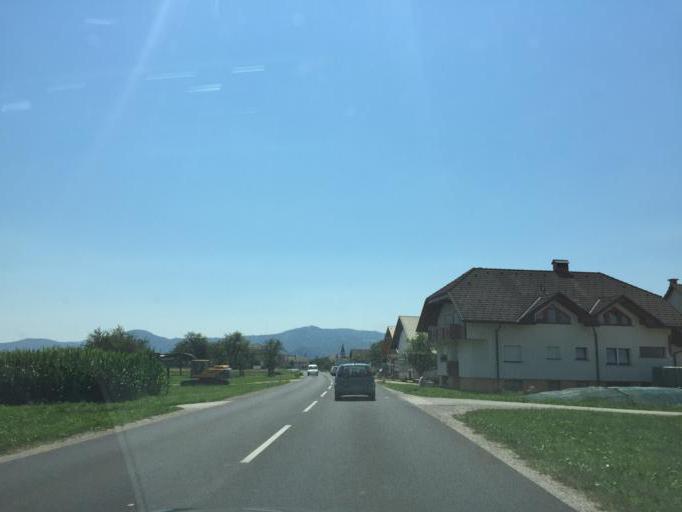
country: SI
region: Skofja Loka
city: Sv. Duh
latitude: 46.2009
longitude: 14.3322
